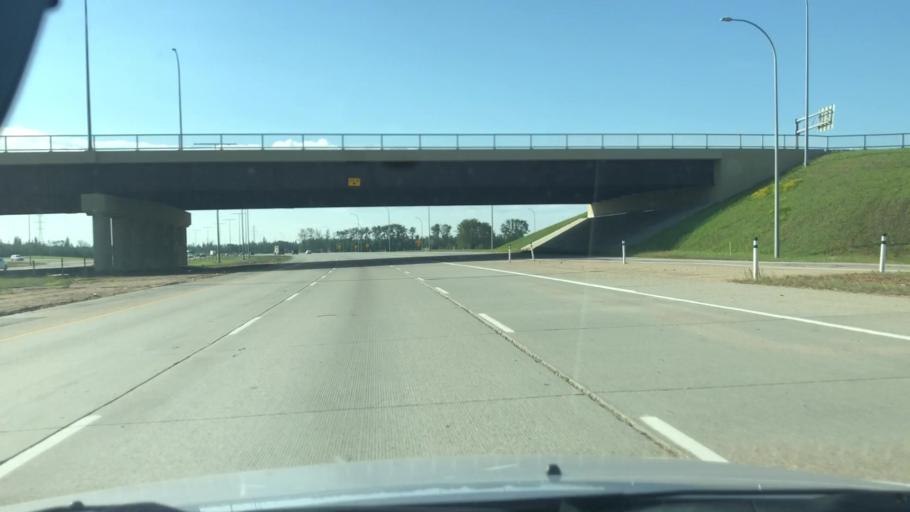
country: CA
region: Alberta
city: Devon
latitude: 53.4806
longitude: -113.6590
